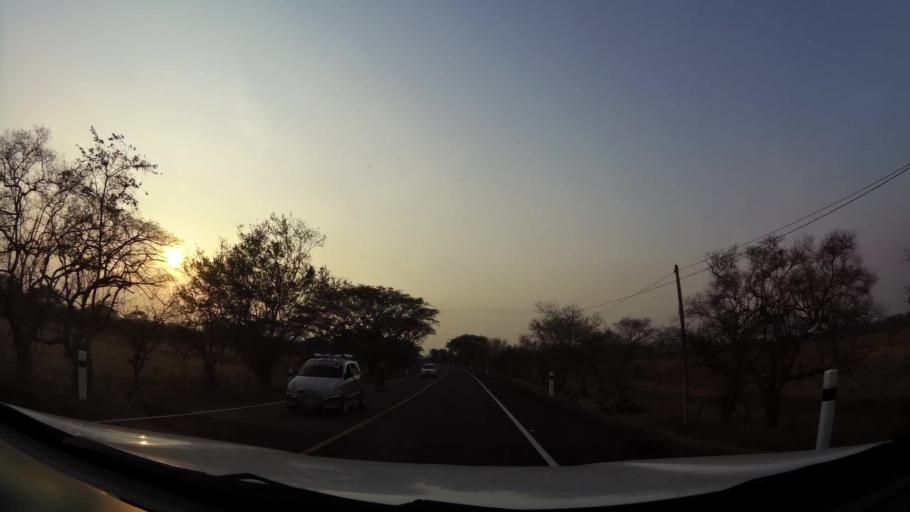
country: NI
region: Leon
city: Nagarote
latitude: 12.3144
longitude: -86.6076
